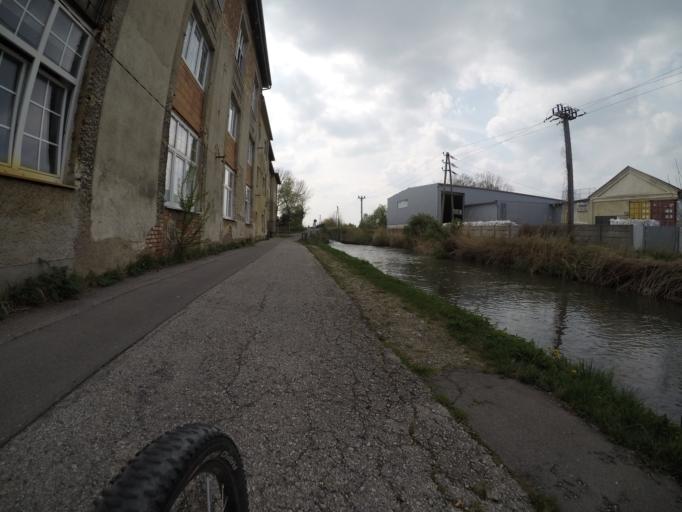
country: AT
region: Lower Austria
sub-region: Politischer Bezirk Baden
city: Pfaffstatten
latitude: 48.0070
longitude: 16.2636
